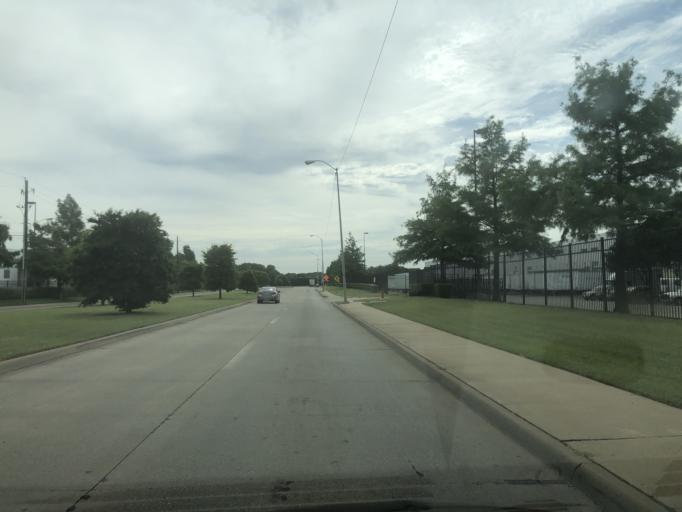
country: US
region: Texas
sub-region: Dallas County
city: Irving
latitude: 32.7984
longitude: -96.9983
